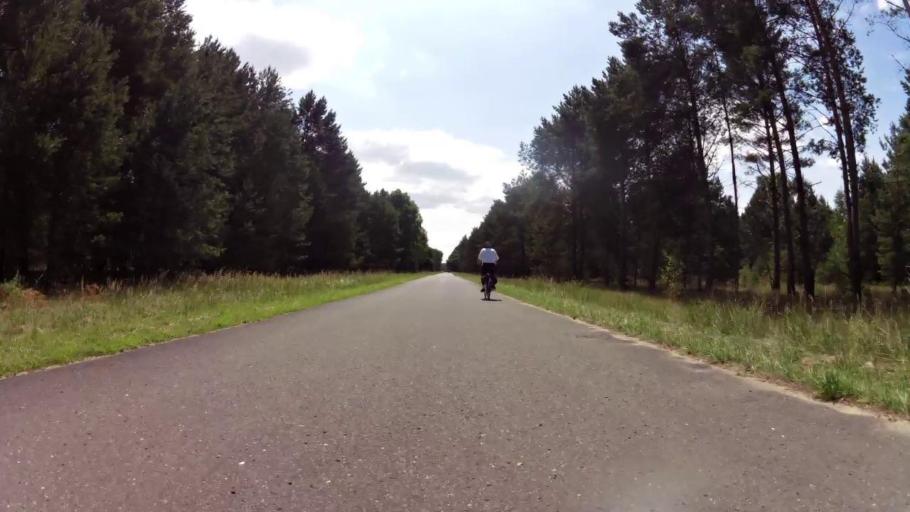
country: PL
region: West Pomeranian Voivodeship
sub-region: Powiat drawski
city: Drawsko Pomorskie
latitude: 53.3896
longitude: 15.7287
